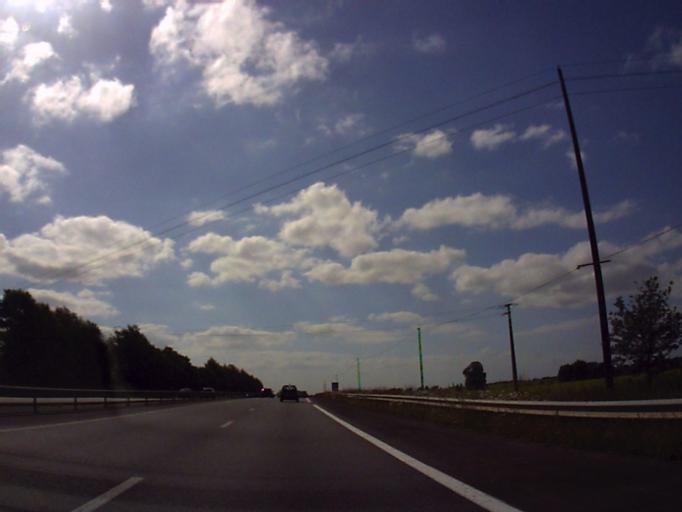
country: FR
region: Brittany
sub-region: Departement d'Ille-et-Vilaine
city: Saint-Gilles
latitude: 48.1617
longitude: -1.8554
